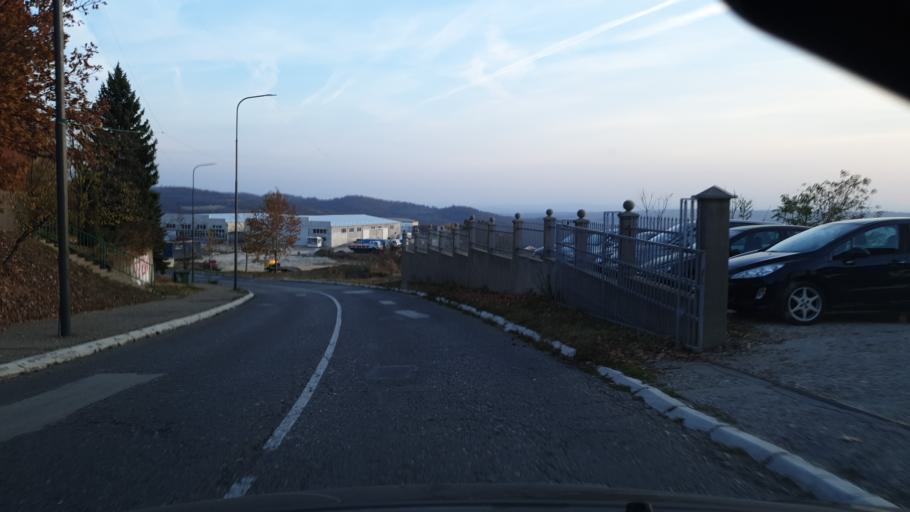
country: RS
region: Central Serbia
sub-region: Borski Okrug
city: Bor
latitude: 44.0551
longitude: 22.0956
